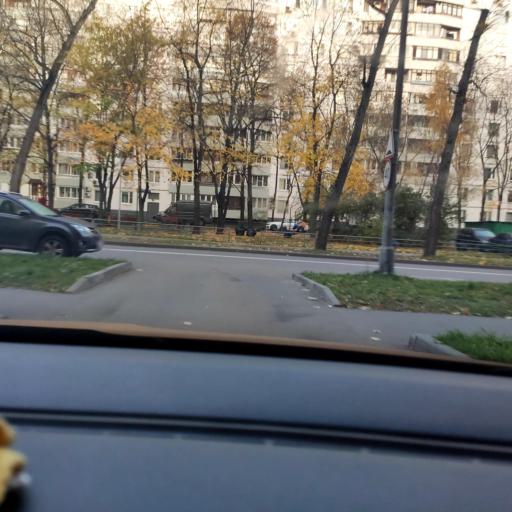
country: RU
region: Moscow
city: Rostokino
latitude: 55.8167
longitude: 37.6603
